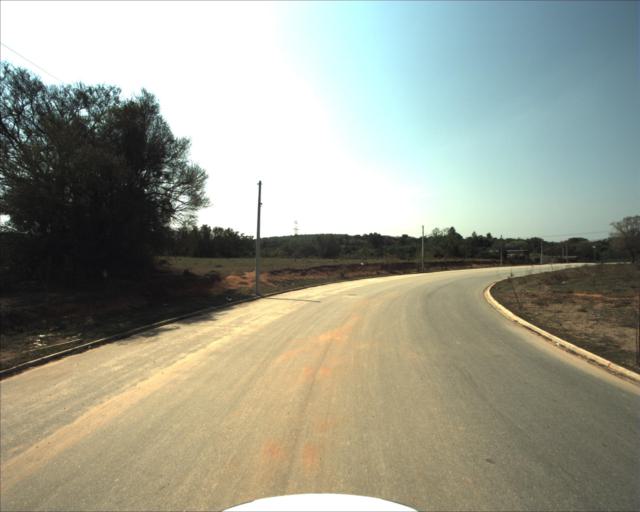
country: BR
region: Sao Paulo
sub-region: Sorocaba
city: Sorocaba
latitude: -23.4196
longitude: -47.4441
